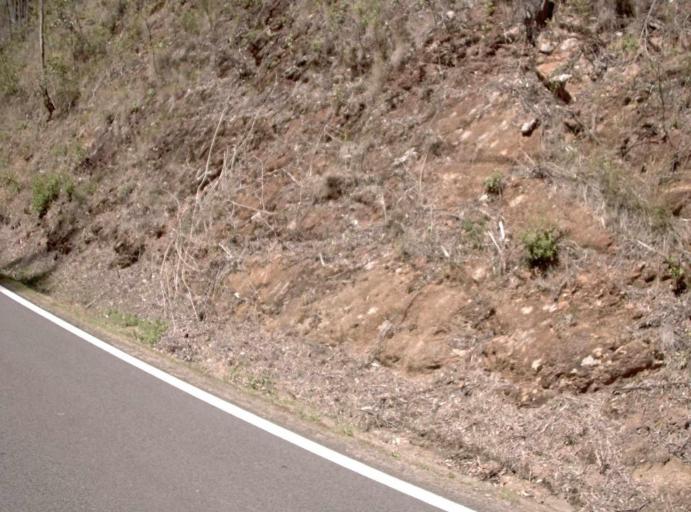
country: AU
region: New South Wales
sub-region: Bombala
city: Bombala
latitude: -37.5838
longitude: 148.9192
